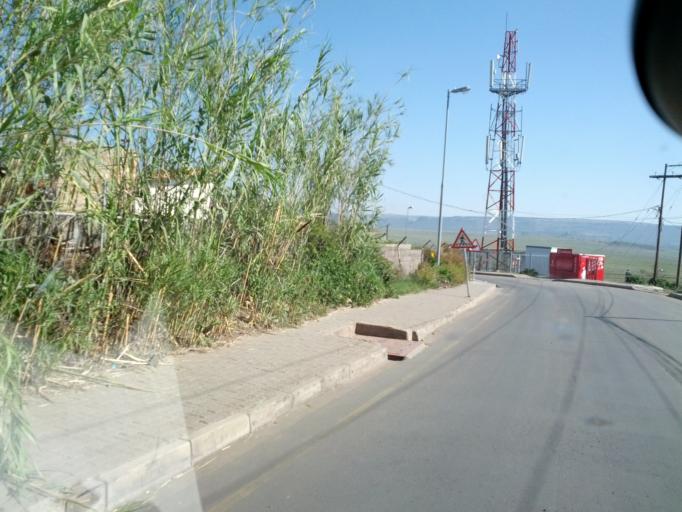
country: LS
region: Maseru
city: Maseru
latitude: -29.3057
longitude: 27.4870
